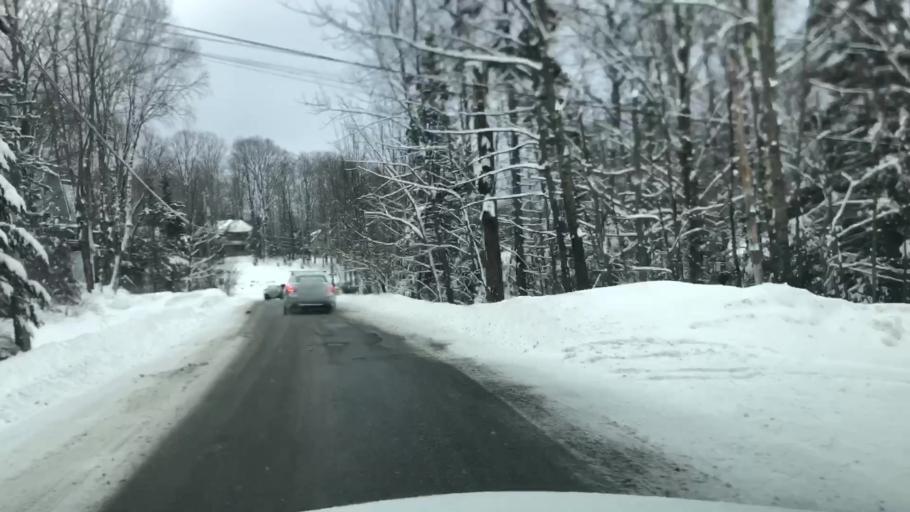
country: US
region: Vermont
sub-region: Rutland County
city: Rutland
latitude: 43.6480
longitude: -72.7864
